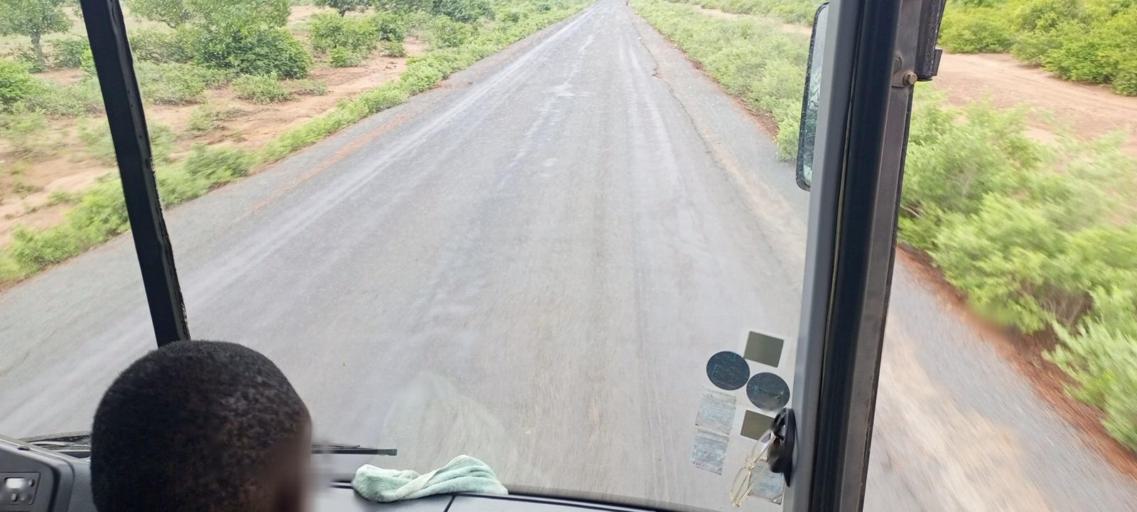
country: ML
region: Sikasso
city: Koutiala
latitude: 12.5722
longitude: -5.6034
